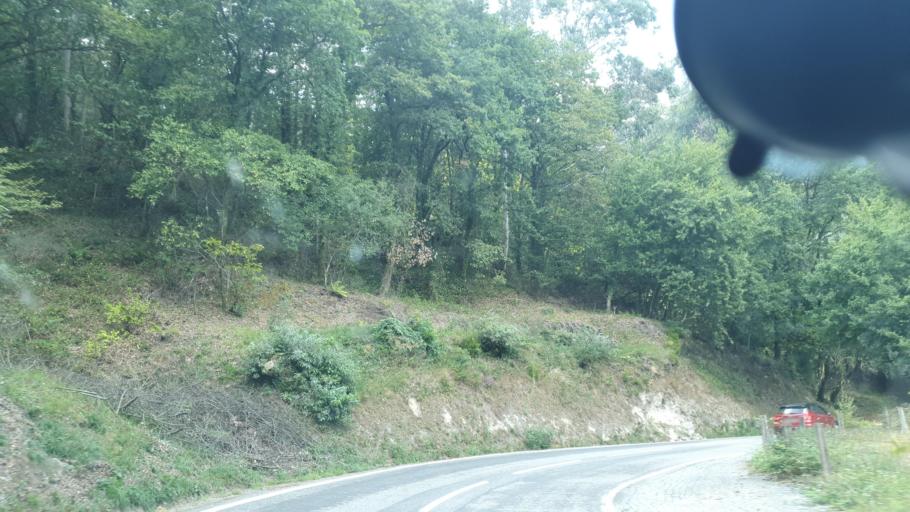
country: PT
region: Braga
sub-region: Vieira do Minho
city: Real
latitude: 41.7095
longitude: -8.2190
